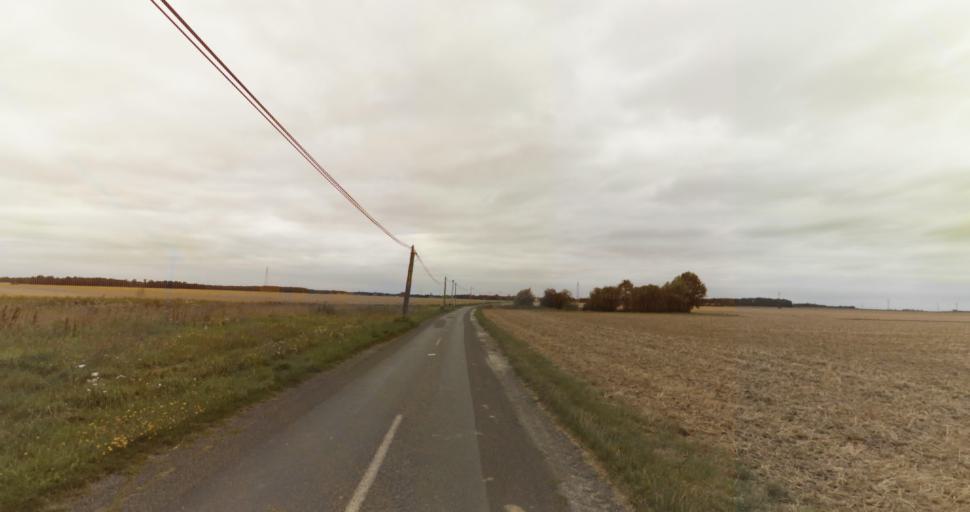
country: FR
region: Haute-Normandie
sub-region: Departement de l'Eure
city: Menilles
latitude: 48.9456
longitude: 1.2663
